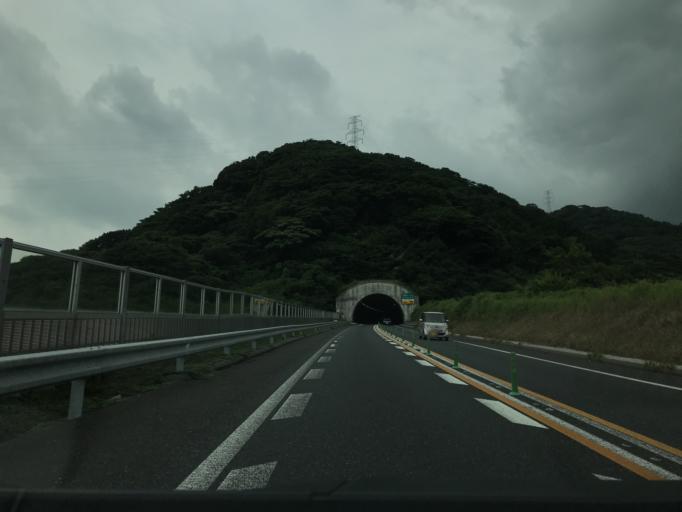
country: JP
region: Fukuoka
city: Kanda
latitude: 33.7785
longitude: 130.9709
